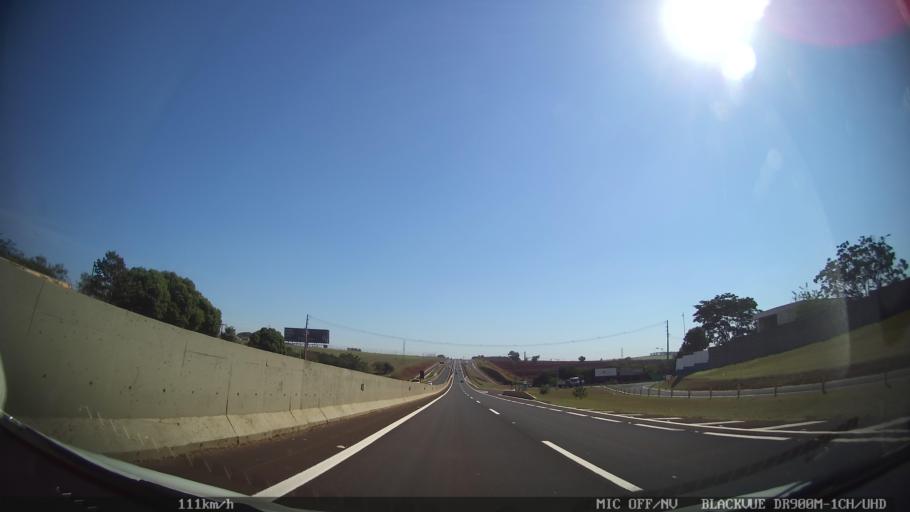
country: BR
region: Sao Paulo
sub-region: Ribeirao Preto
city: Ribeirao Preto
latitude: -21.2060
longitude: -47.8588
